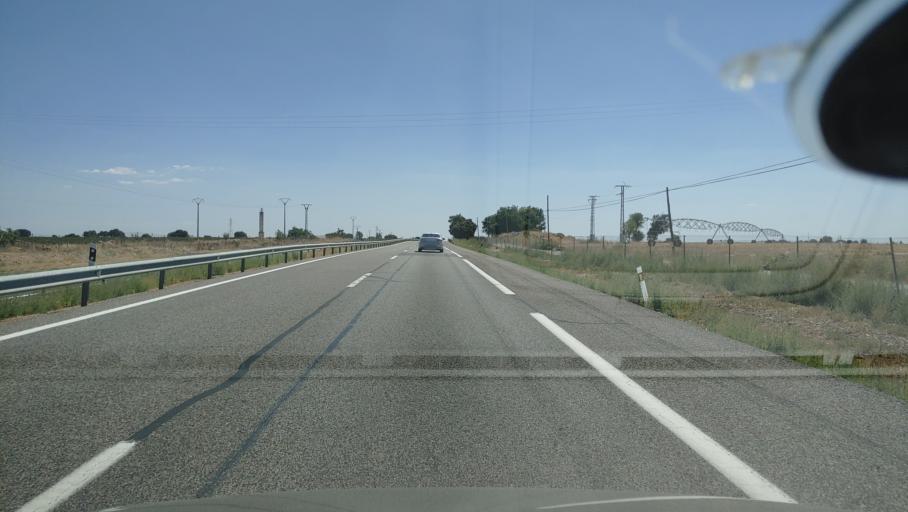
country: ES
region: Castille-La Mancha
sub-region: Provincia de Ciudad Real
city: Villarta de San Juan
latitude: 39.1989
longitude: -3.4052
